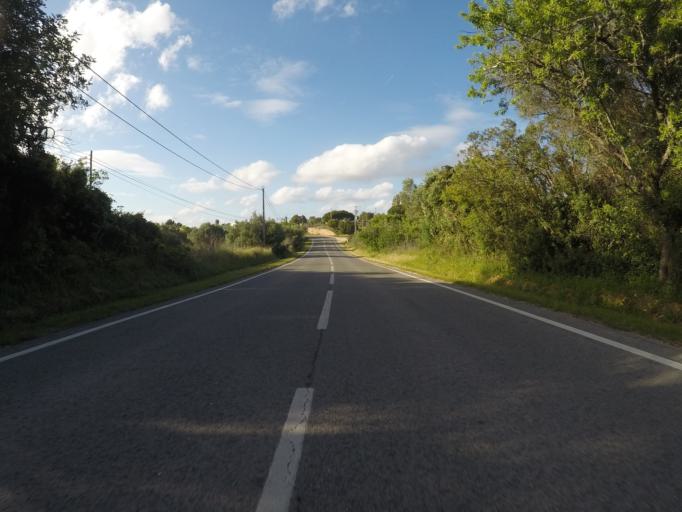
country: PT
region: Faro
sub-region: Lagoa
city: Carvoeiro
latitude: 37.1092
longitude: -8.4459
